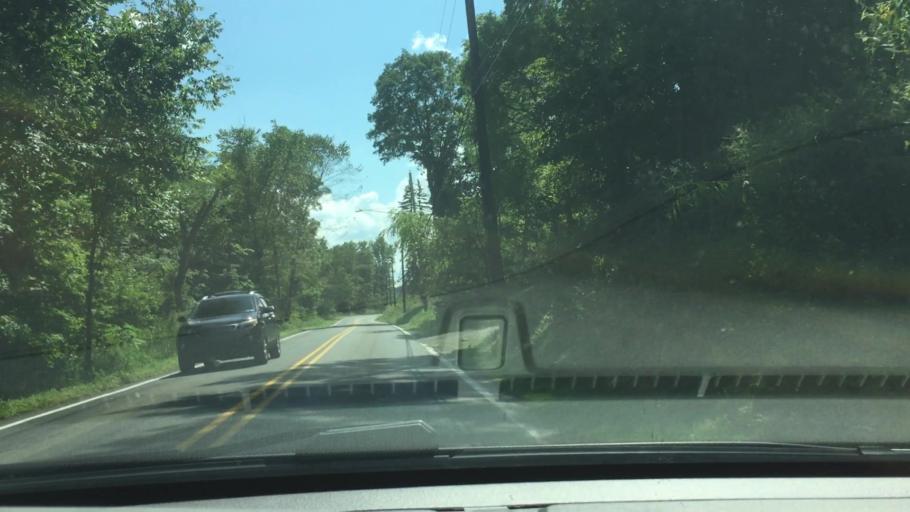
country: US
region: Pennsylvania
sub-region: Lawrence County
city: New Wilmington
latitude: 41.1115
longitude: -80.4379
